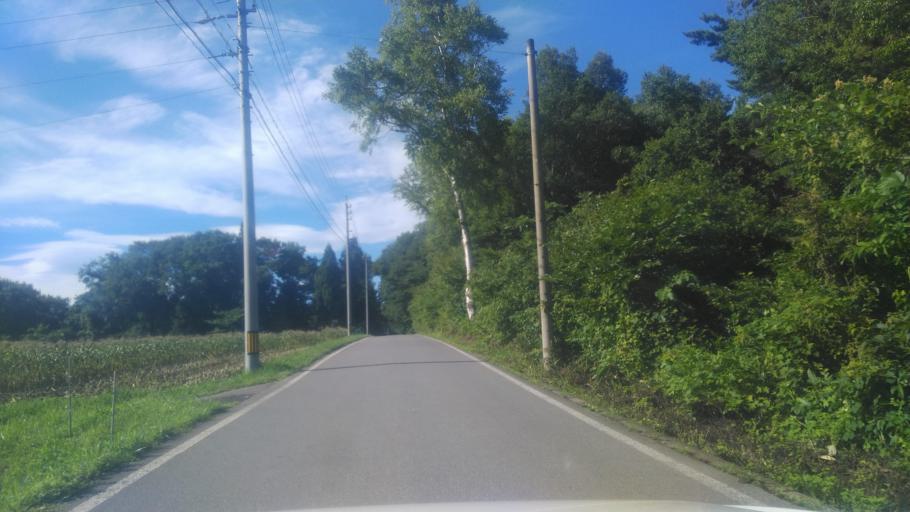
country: JP
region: Nagano
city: Nagano-shi
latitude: 36.7914
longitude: 138.1788
